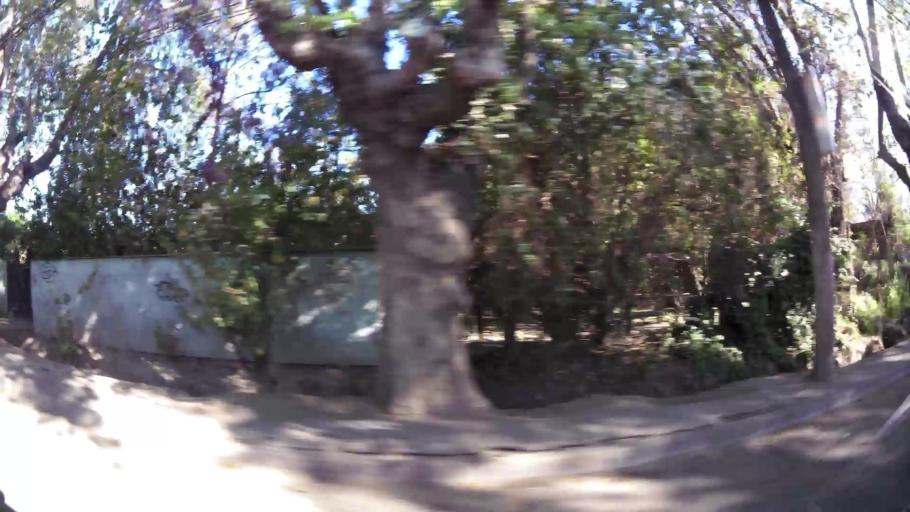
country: CL
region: Santiago Metropolitan
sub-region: Provincia de Talagante
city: Penaflor
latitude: -33.6104
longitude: -70.8689
